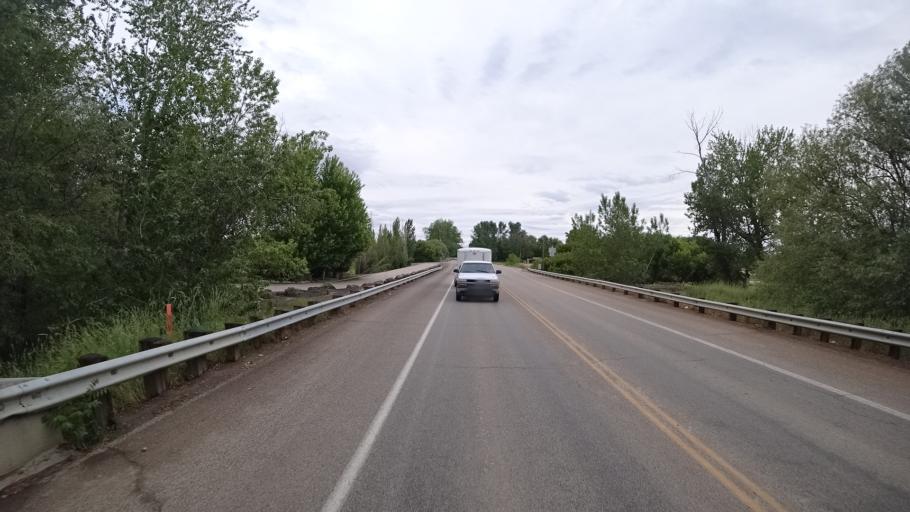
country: US
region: Idaho
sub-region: Ada County
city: Star
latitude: 43.6811
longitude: -116.4933
